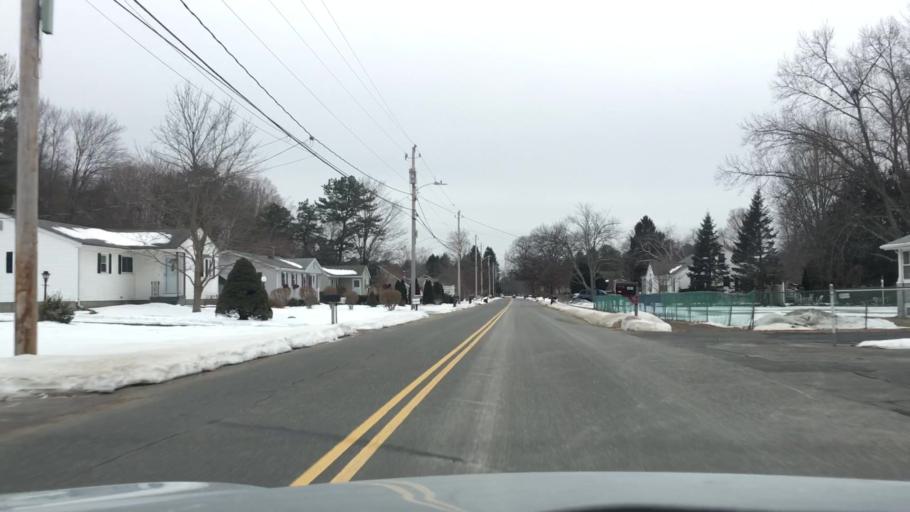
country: US
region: Massachusetts
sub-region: Hampshire County
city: Southampton
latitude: 42.1839
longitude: -72.6805
